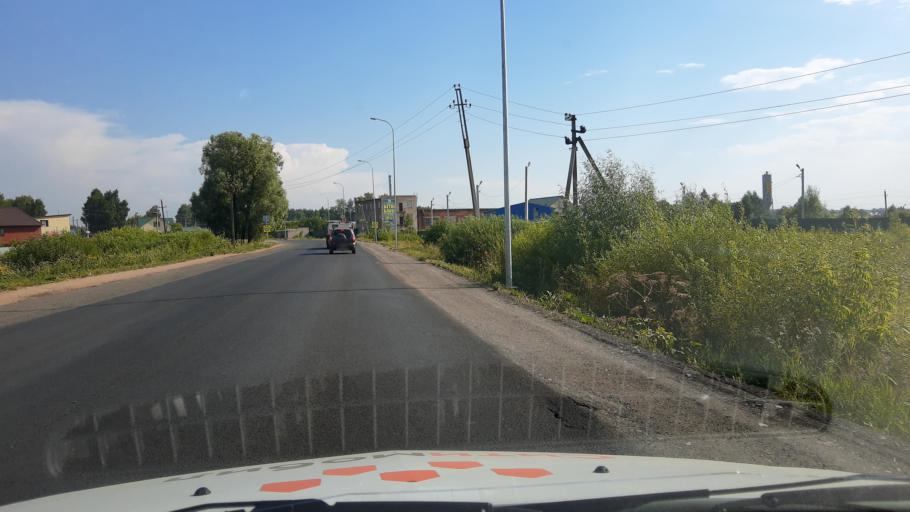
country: RU
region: Bashkortostan
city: Iglino
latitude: 54.8307
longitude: 56.3910
